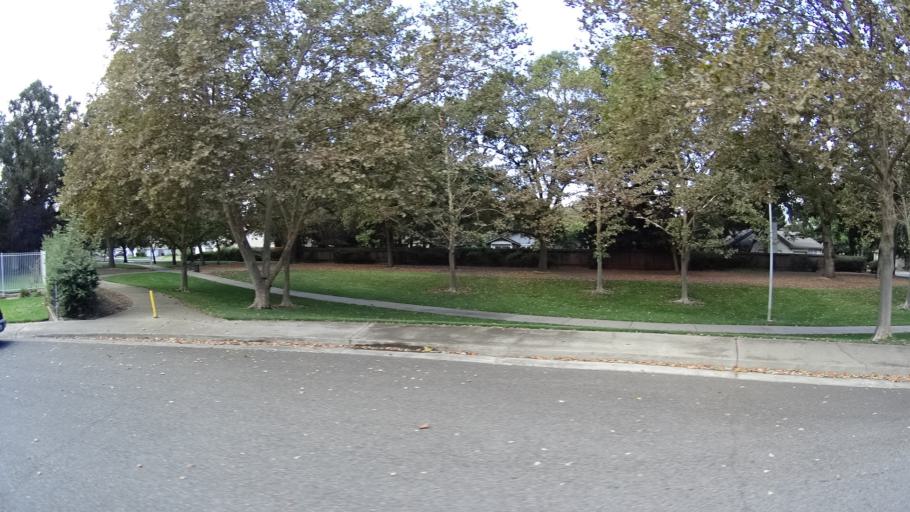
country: US
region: California
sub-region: Sacramento County
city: Laguna
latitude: 38.4167
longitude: -121.4266
